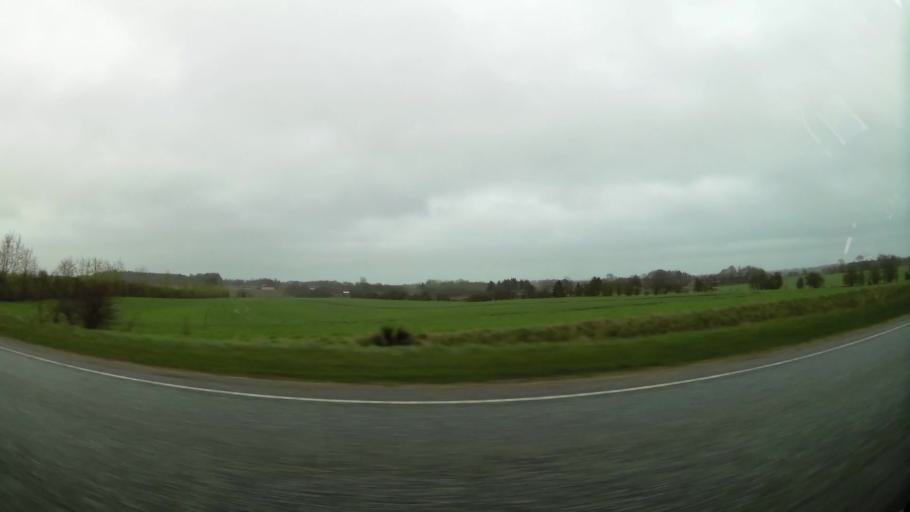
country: DK
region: Central Jutland
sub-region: Herning Kommune
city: Avlum
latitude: 56.2718
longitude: 8.7646
